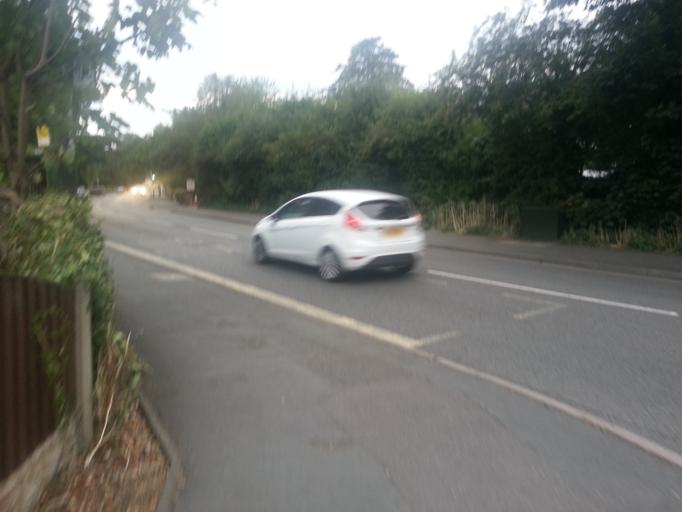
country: GB
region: England
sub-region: Derbyshire
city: Borrowash
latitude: 52.8923
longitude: -1.4238
